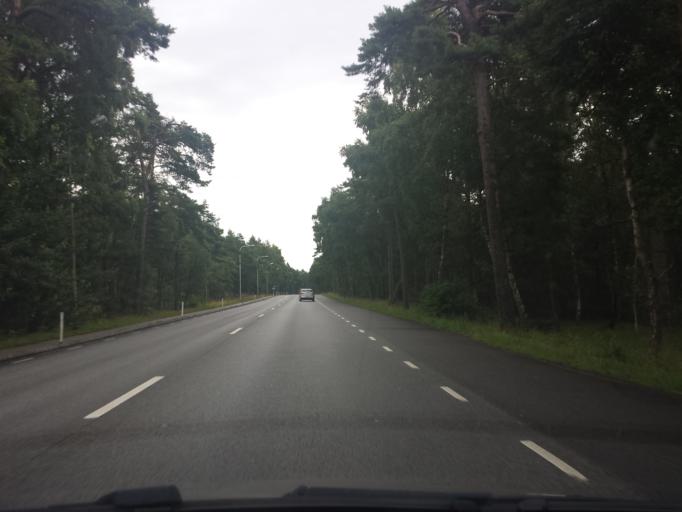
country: SE
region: Skane
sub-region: Ystads Kommun
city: Kopingebro
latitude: 55.4353
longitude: 13.8825
